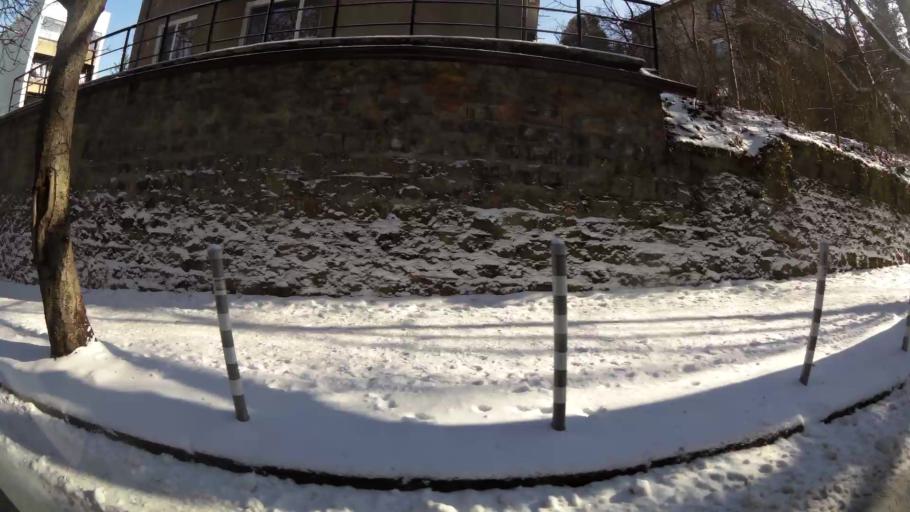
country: BG
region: Sofia-Capital
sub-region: Stolichna Obshtina
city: Sofia
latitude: 42.6765
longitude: 23.3269
